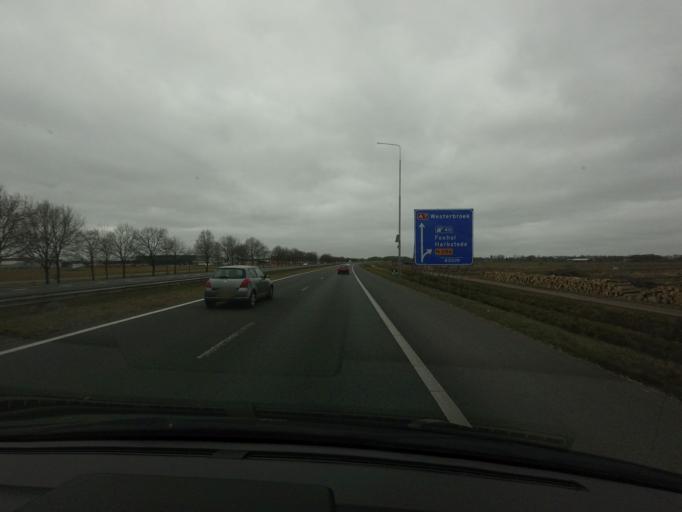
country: NL
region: Groningen
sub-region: Gemeente Hoogezand-Sappemeer
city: Hoogezand
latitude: 53.1723
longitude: 6.7470
